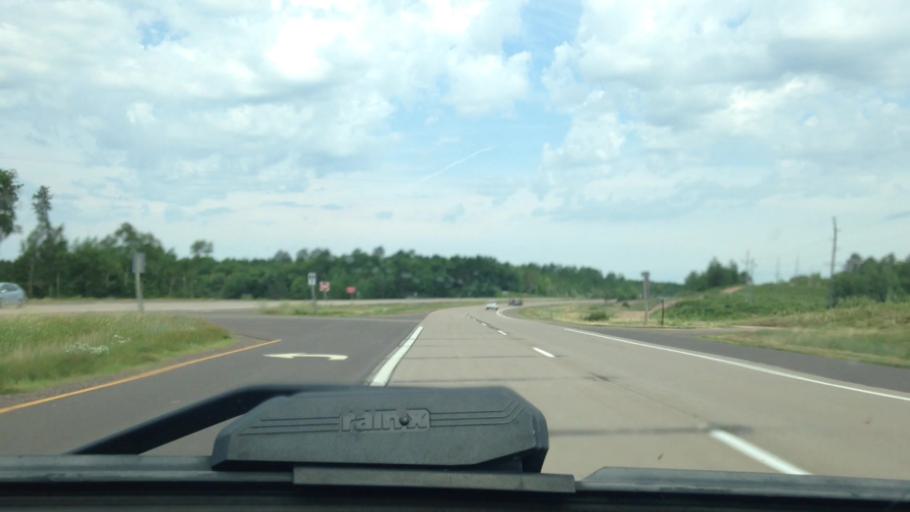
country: US
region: Wisconsin
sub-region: Douglas County
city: Lake Nebagamon
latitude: 46.2168
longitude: -91.7983
